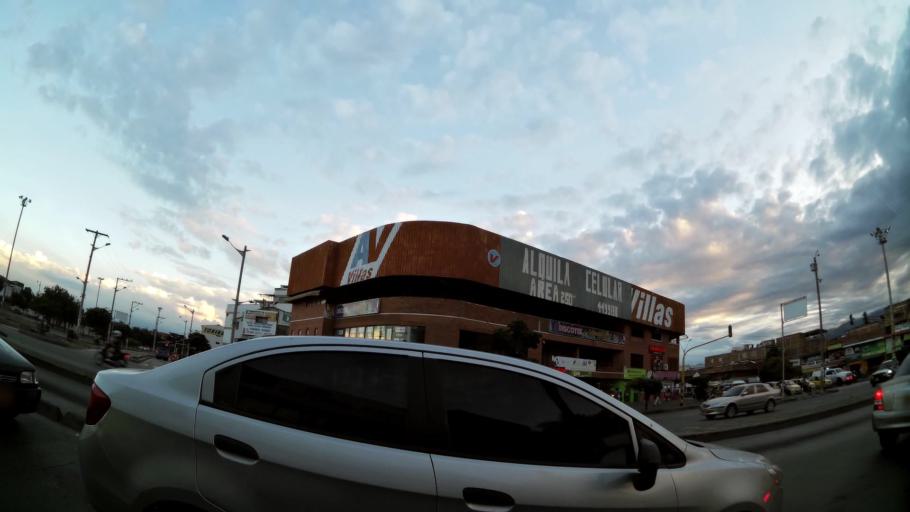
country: CO
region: Valle del Cauca
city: Cali
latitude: 3.4426
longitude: -76.5256
